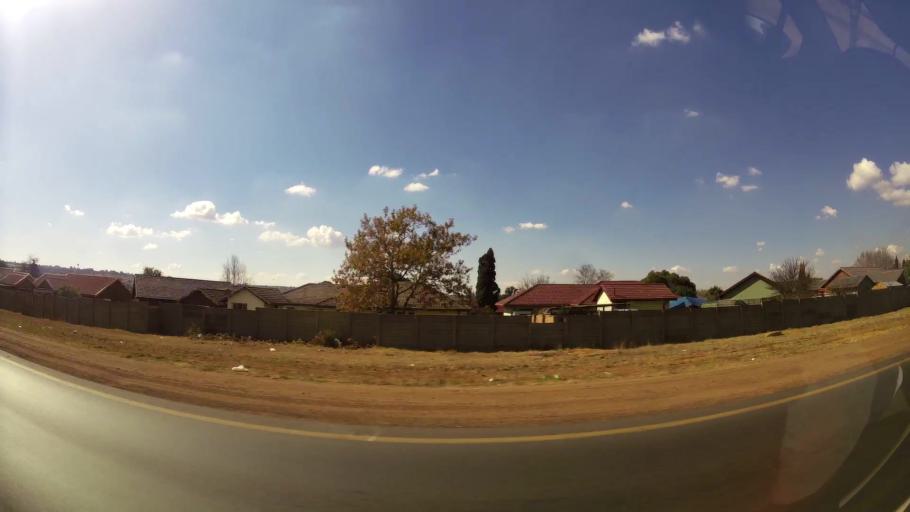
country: ZA
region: Mpumalanga
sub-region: Nkangala District Municipality
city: Witbank
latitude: -25.9428
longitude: 29.2432
